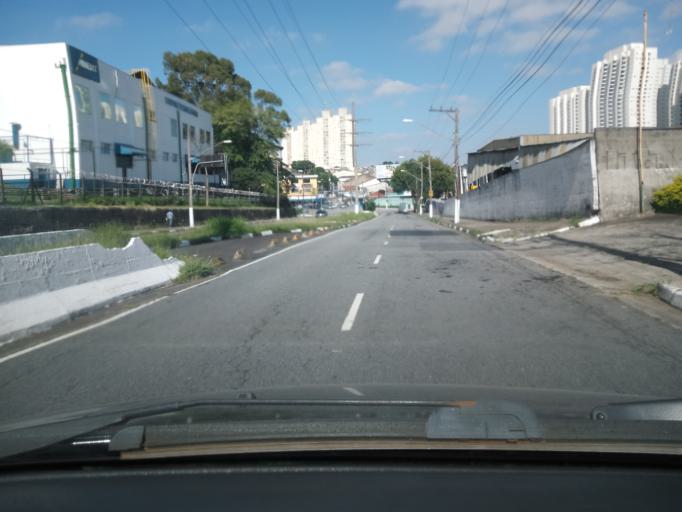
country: BR
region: Sao Paulo
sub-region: Sao Bernardo Do Campo
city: Sao Bernardo do Campo
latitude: -23.6976
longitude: -46.5765
